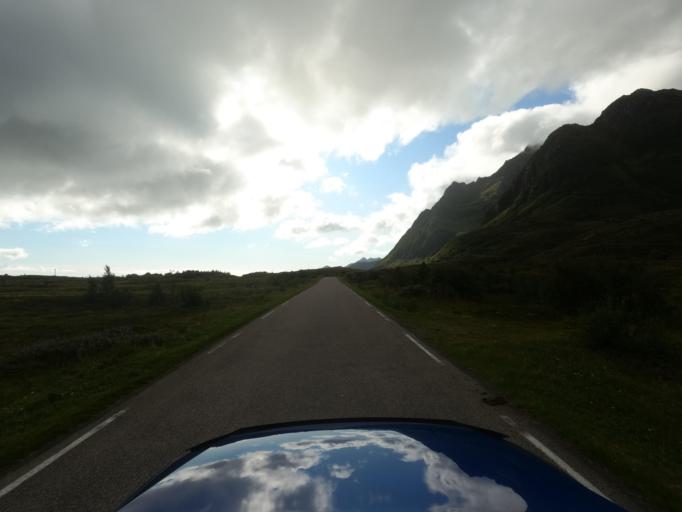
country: NO
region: Nordland
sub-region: Vestvagoy
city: Evjen
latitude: 68.1884
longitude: 13.8595
